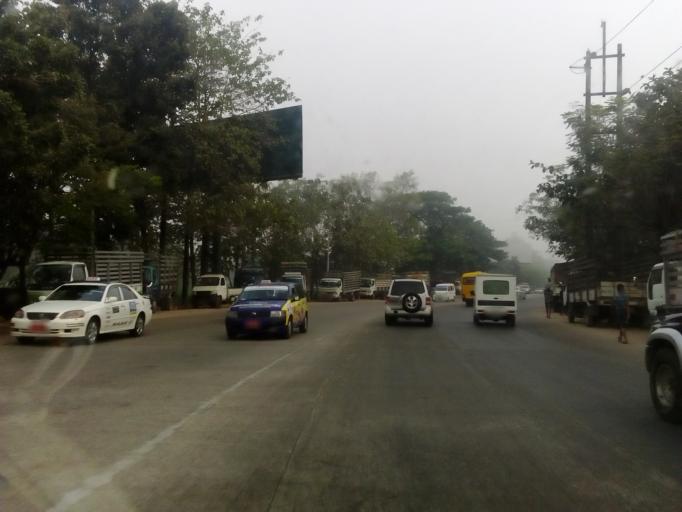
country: MM
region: Yangon
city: Yangon
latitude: 16.8073
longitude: 96.1832
